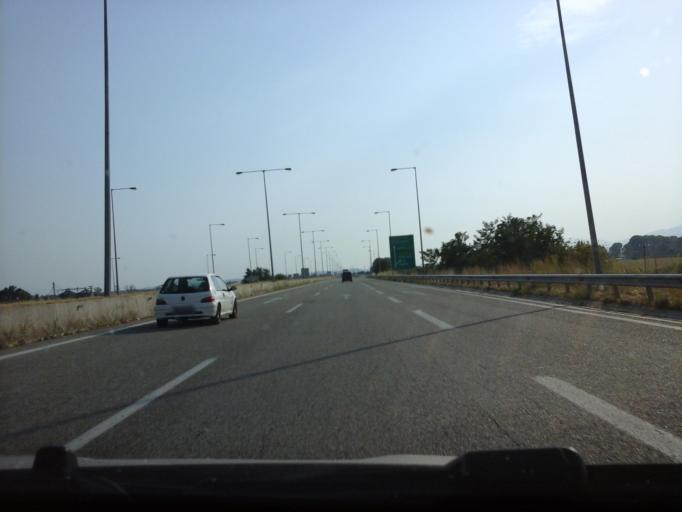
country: GR
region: East Macedonia and Thrace
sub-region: Nomos Xanthis
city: Genissea
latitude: 41.0964
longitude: 24.9438
